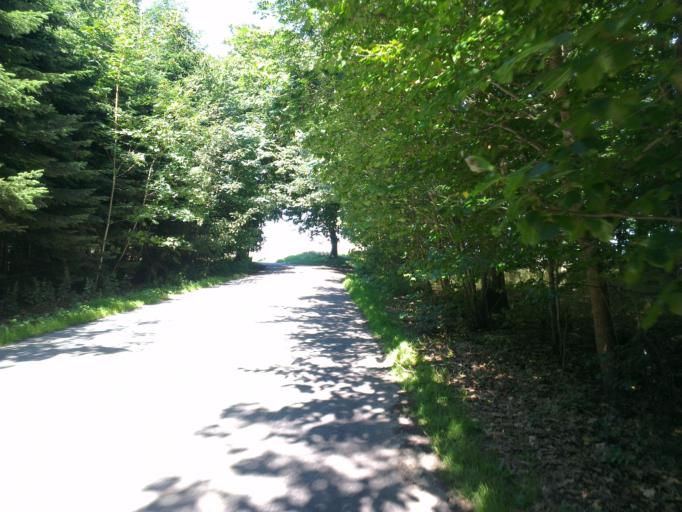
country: DK
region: Capital Region
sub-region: Frederikssund Kommune
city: Skibby
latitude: 55.7198
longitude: 11.9516
